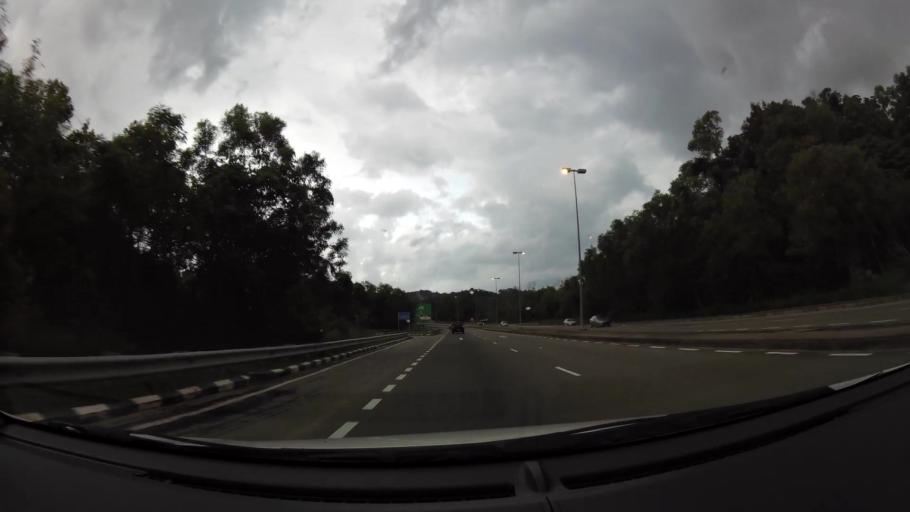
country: BN
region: Brunei and Muara
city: Bandar Seri Begawan
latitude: 4.9347
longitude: 114.9724
